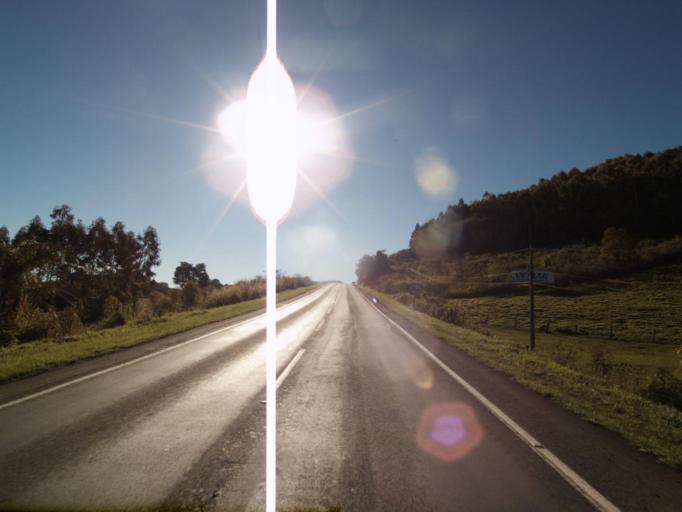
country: AR
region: Misiones
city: Bernardo de Irigoyen
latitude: -26.4818
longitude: -53.5040
